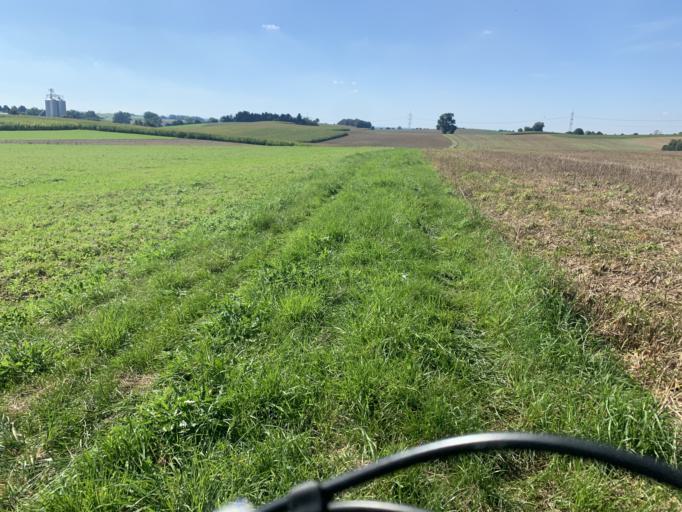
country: DE
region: Bavaria
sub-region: Swabia
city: Ried
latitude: 48.2940
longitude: 11.0172
